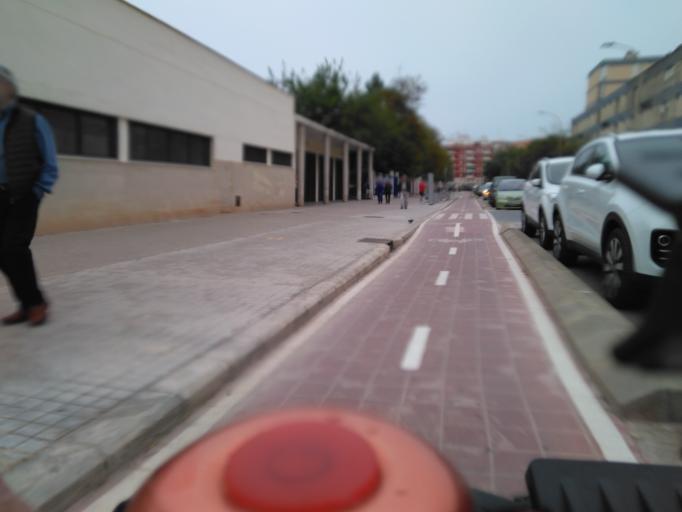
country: ES
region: Valencia
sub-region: Provincia de Valencia
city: Valencia
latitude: 39.4658
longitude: -0.3974
